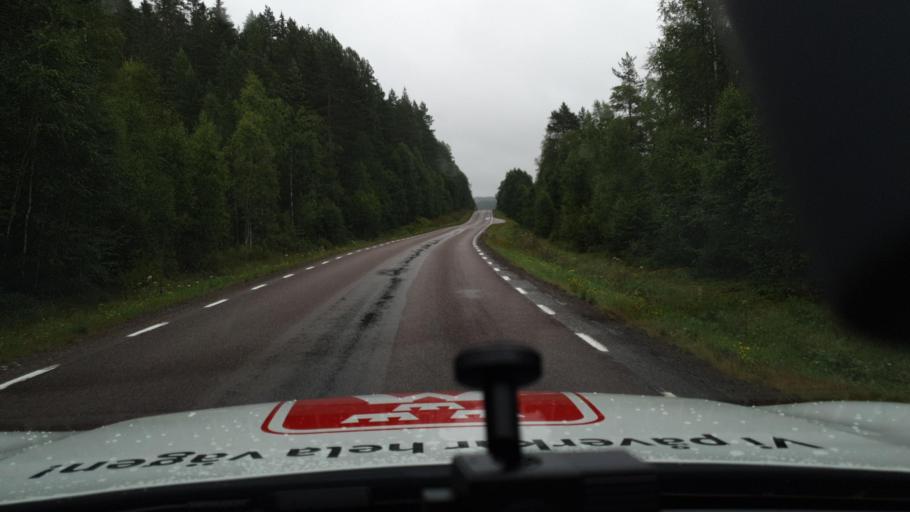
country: SE
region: Vaermland
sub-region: Torsby Kommun
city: Torsby
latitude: 59.9355
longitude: 12.7897
